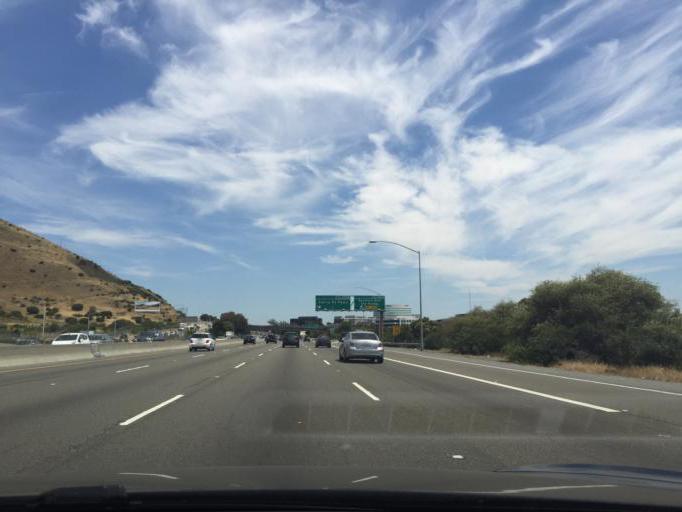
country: US
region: California
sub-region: San Mateo County
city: Brisbane
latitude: 37.6673
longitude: -122.3950
